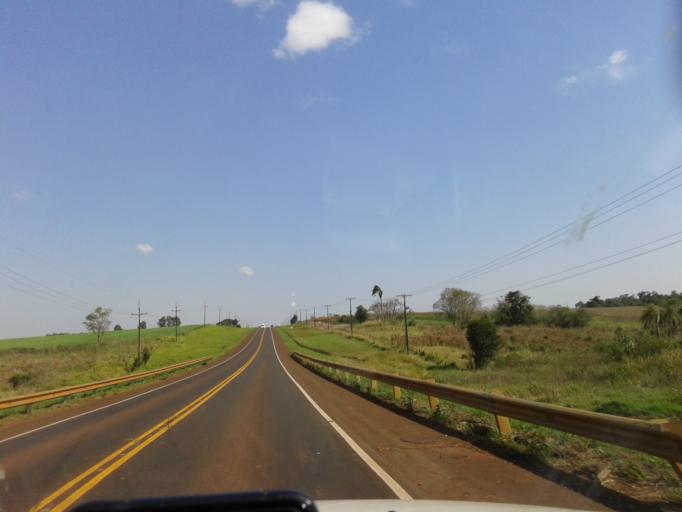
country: PY
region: Alto Parana
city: Colonia Yguazu
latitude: -25.6180
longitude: -54.9526
